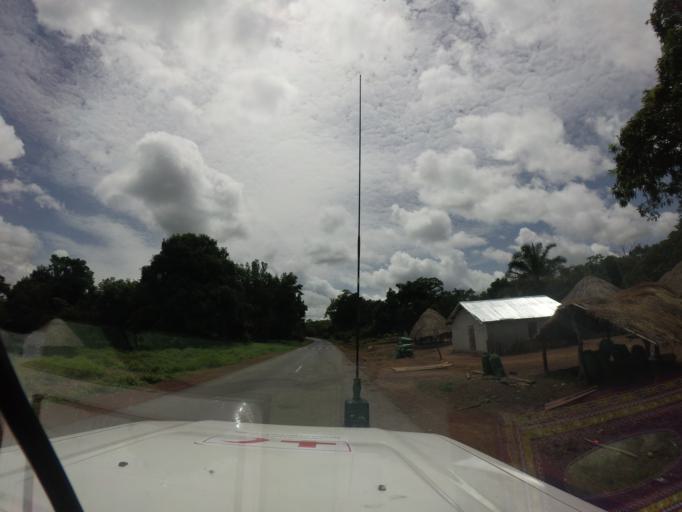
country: SL
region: Northern Province
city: Gberia Fotombu
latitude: 10.1303
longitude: -11.1615
